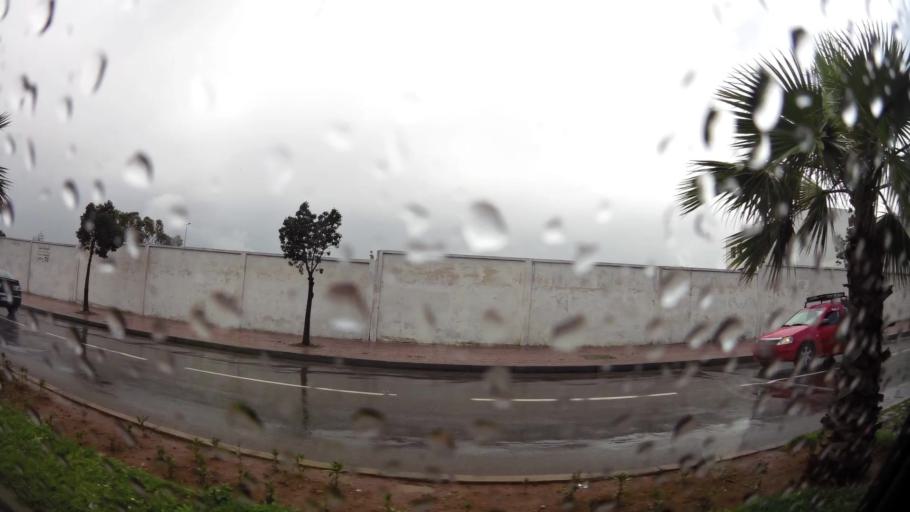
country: MA
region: Grand Casablanca
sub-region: Casablanca
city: Casablanca
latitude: 33.5503
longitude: -7.6709
